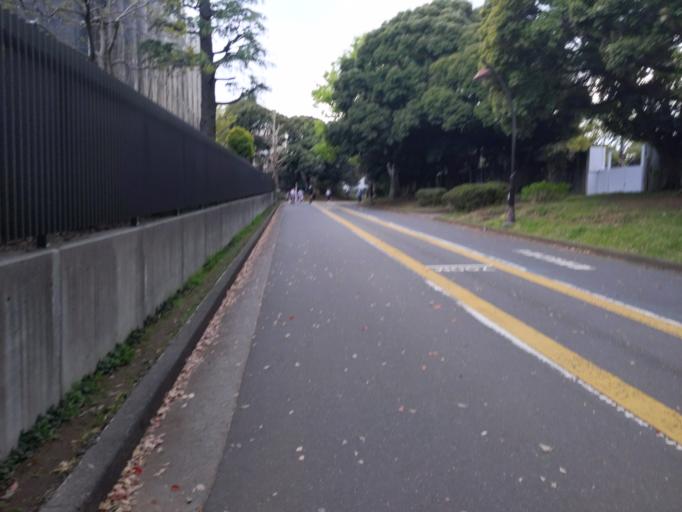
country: JP
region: Tokyo
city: Tokyo
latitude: 35.6217
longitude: 139.6637
